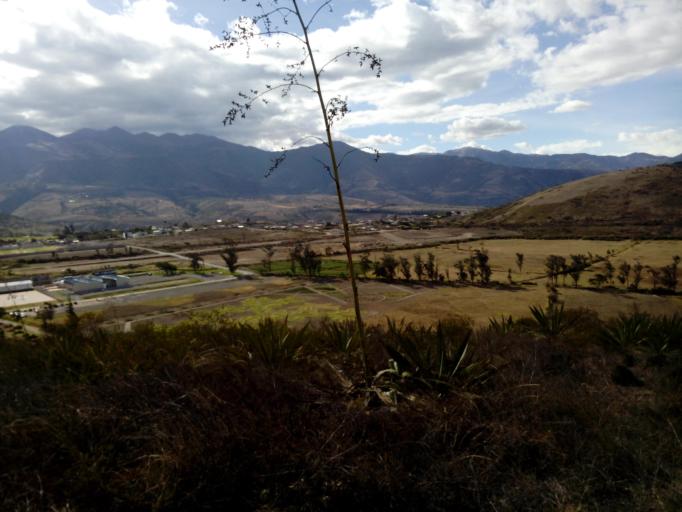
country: EC
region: Imbabura
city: Atuntaqui
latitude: 0.4181
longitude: -78.1860
